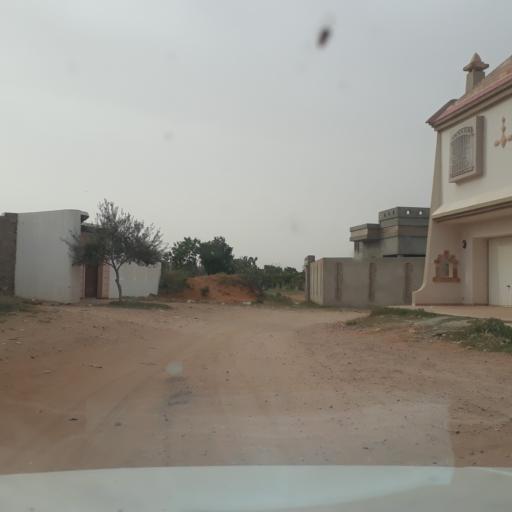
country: TN
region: Safaqis
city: Al Qarmadah
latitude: 34.8259
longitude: 10.7750
